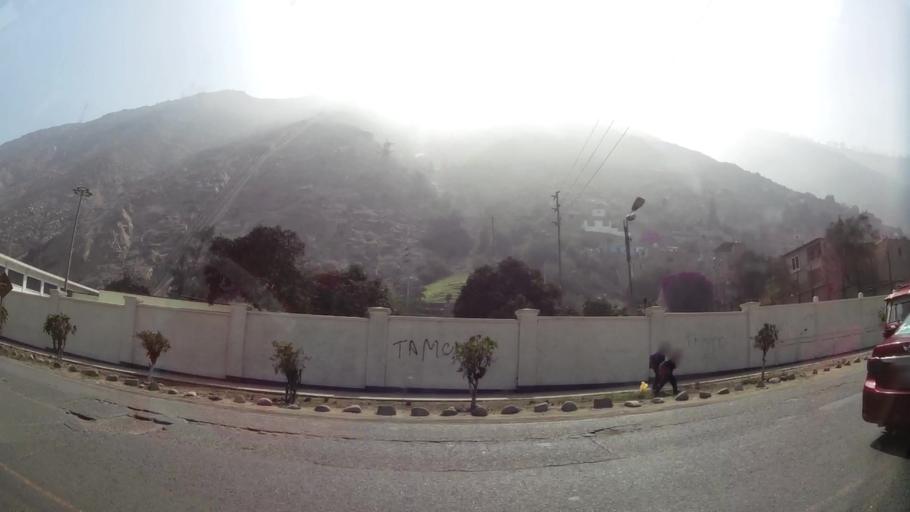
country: PE
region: Lima
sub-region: Lima
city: Asentamiento Humano Nicolas de Pierola
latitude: -11.9275
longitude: -76.6885
